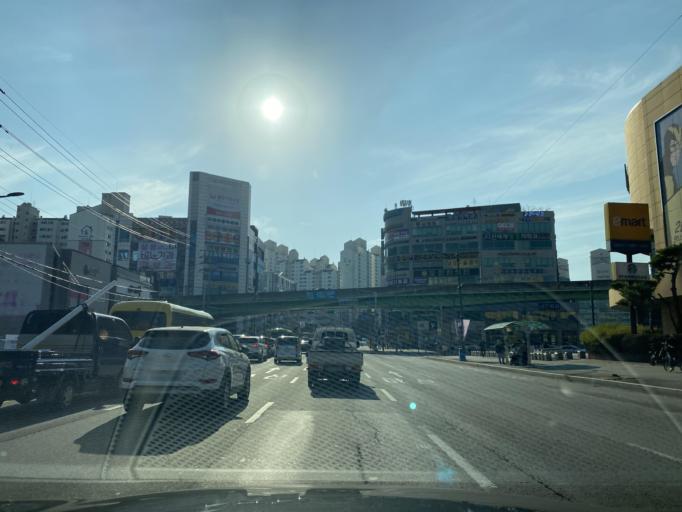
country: KR
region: Chungcheongnam-do
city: Cheonan
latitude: 36.7955
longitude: 127.1279
